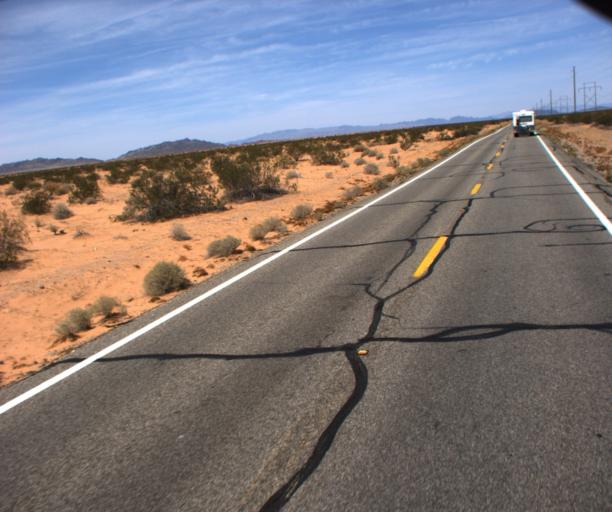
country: US
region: Arizona
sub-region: La Paz County
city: Quartzsite
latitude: 33.8958
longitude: -114.2169
